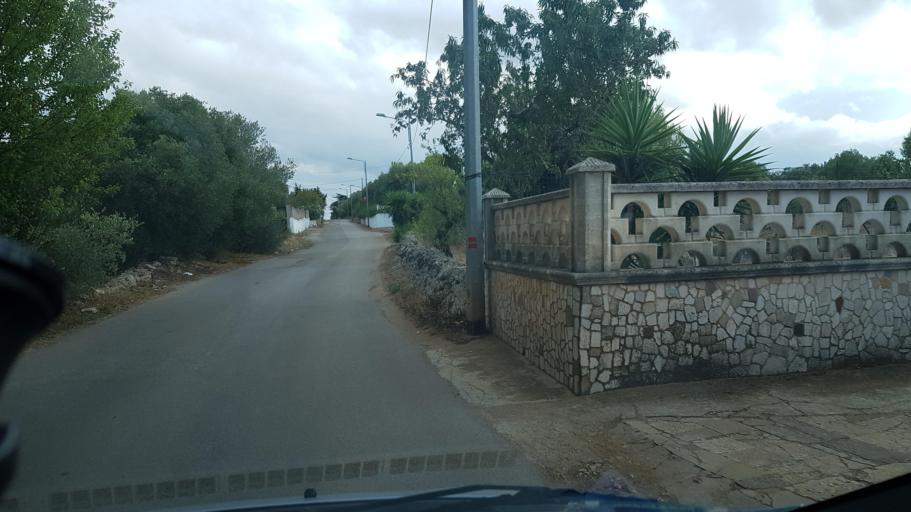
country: IT
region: Apulia
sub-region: Provincia di Brindisi
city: San Vito dei Normanni
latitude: 40.6666
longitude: 17.7160
